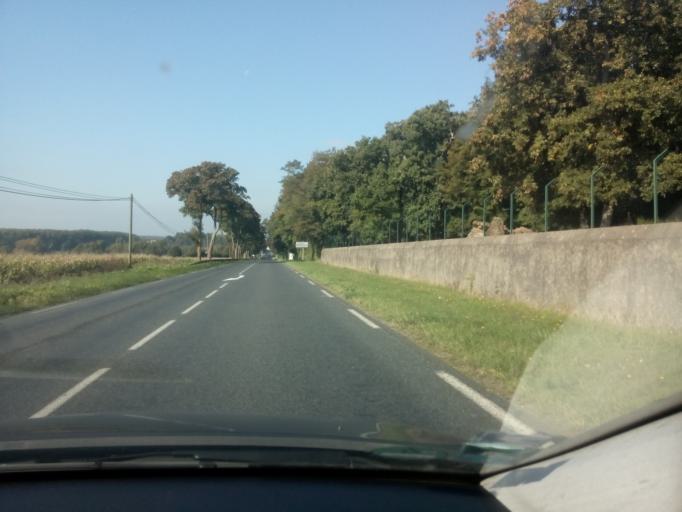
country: FR
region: Pays de la Loire
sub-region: Departement de Maine-et-Loire
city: Seiches-sur-le-Loir
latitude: 47.5701
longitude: -0.3426
